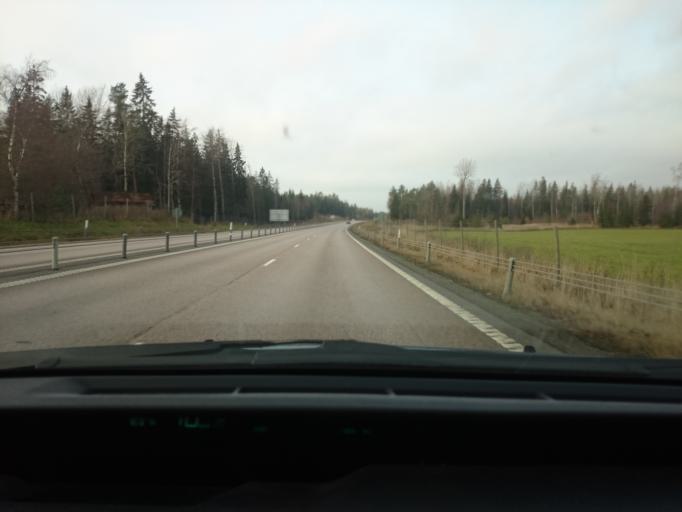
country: SE
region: Vaestmanland
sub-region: Sala Kommun
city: Sala
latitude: 59.8894
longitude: 16.5590
